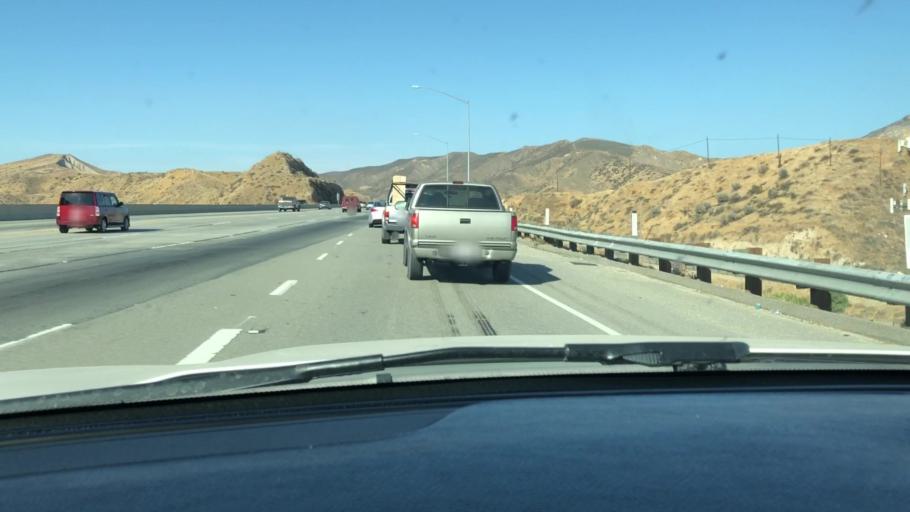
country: US
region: California
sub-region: Los Angeles County
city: Agua Dulce
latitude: 34.4349
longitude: -118.3813
